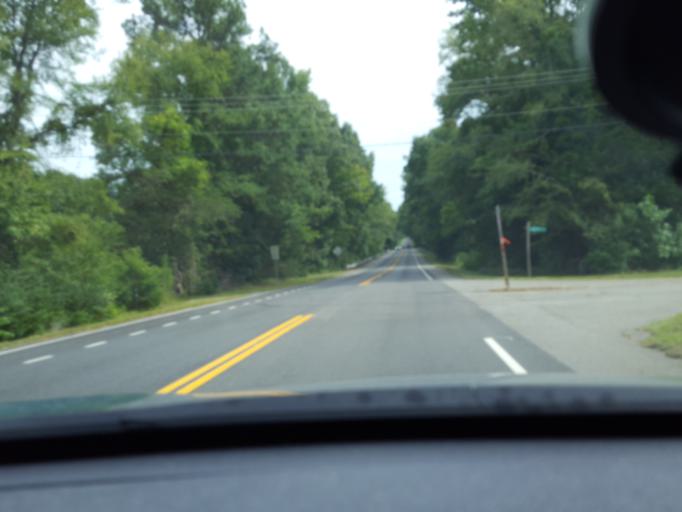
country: US
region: Virginia
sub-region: Hanover County
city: Hanover
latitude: 37.7605
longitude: -77.3657
